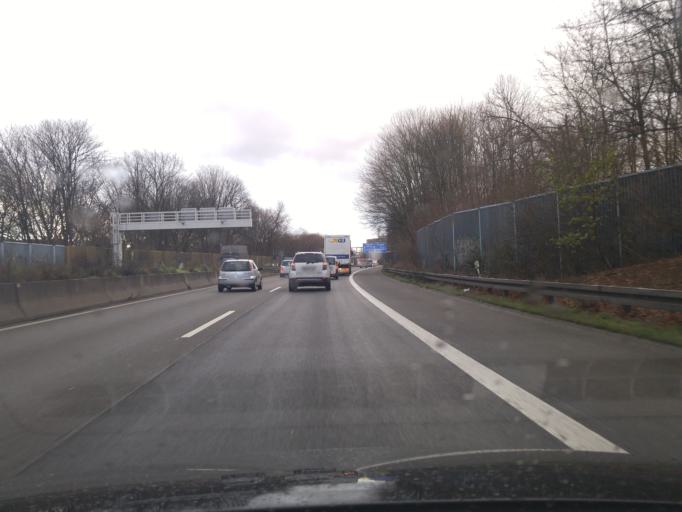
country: DE
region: North Rhine-Westphalia
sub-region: Regierungsbezirk Arnsberg
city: Bochum
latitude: 51.4953
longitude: 7.2443
